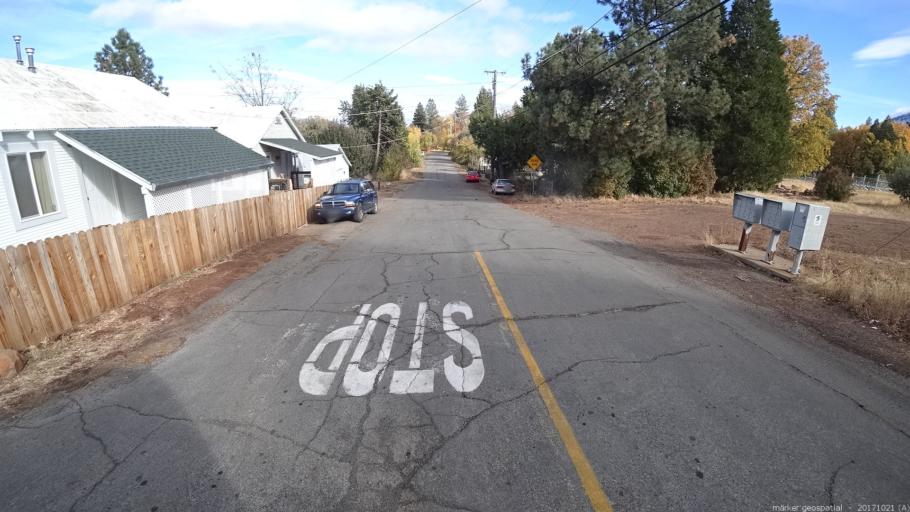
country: US
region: California
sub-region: Shasta County
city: Burney
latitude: 40.8808
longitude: -121.6718
